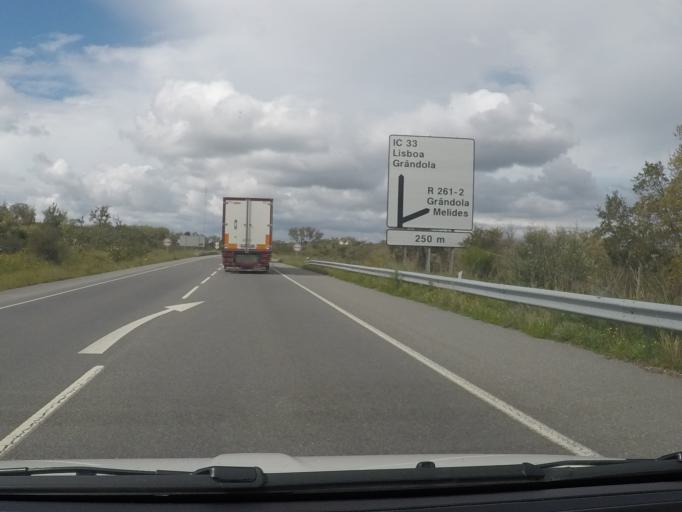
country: PT
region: Setubal
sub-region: Grandola
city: Grandola
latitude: 38.1516
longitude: -8.6496
